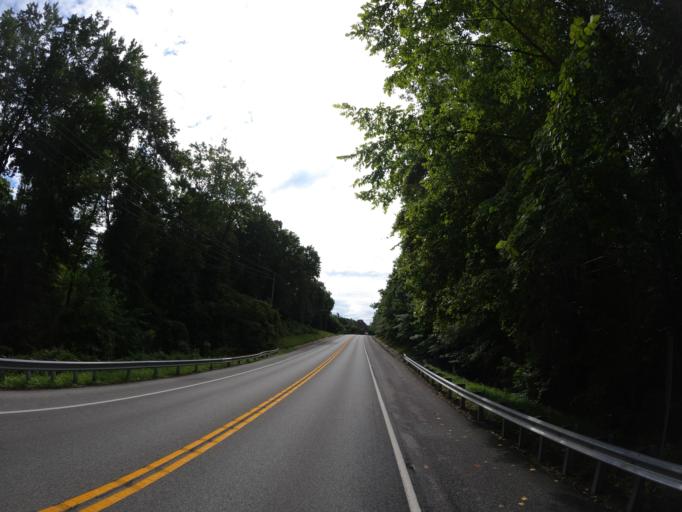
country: US
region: Maryland
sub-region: Saint Mary's County
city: Mechanicsville
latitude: 38.3709
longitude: -76.6892
